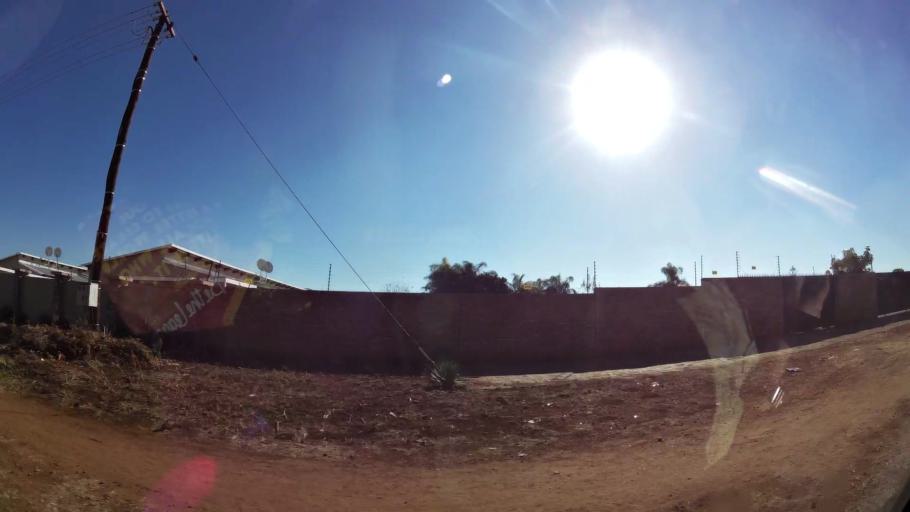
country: ZA
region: Limpopo
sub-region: Waterberg District Municipality
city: Mokopane
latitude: -24.1808
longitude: 28.9983
